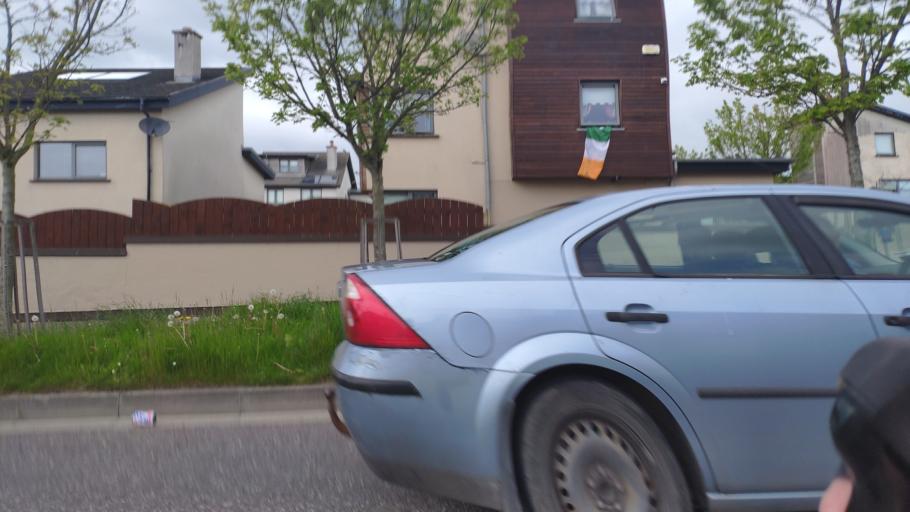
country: IE
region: Munster
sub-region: County Cork
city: Cork
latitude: 51.9057
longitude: -8.5028
